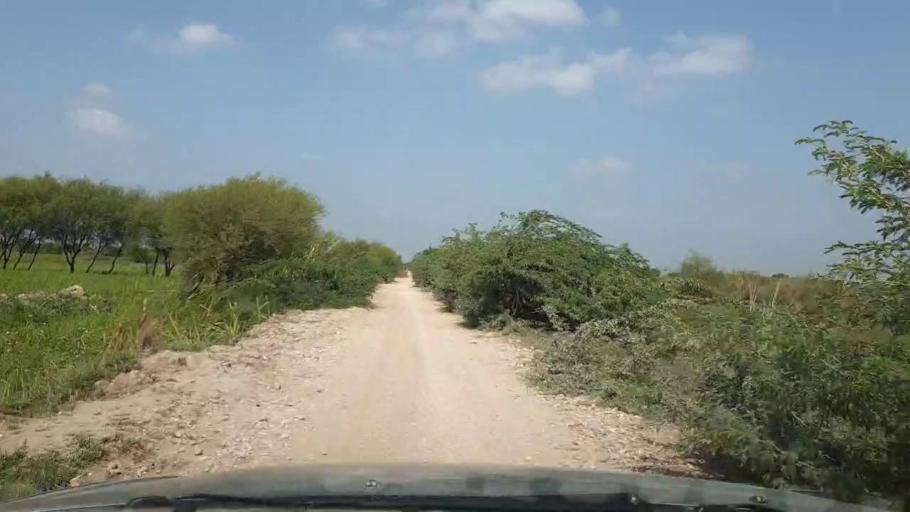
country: PK
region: Sindh
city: Rajo Khanani
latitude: 25.0216
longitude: 68.9165
